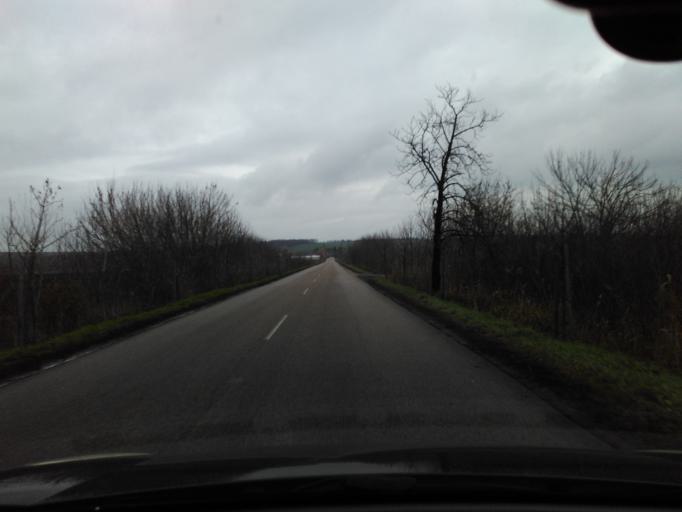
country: HU
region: Heves
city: Hatvan
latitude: 47.6955
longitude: 19.6807
